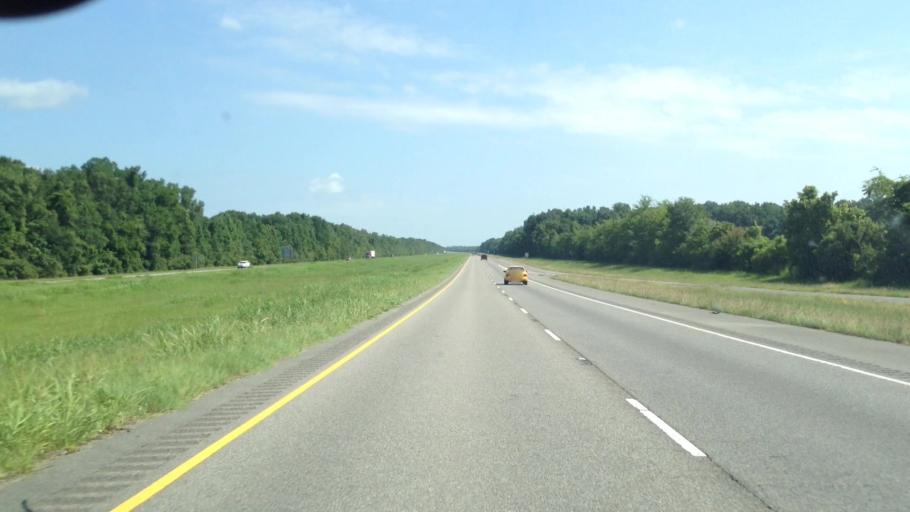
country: US
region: Louisiana
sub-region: Avoyelles Parish
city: Bunkie
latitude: 30.8684
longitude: -92.2276
